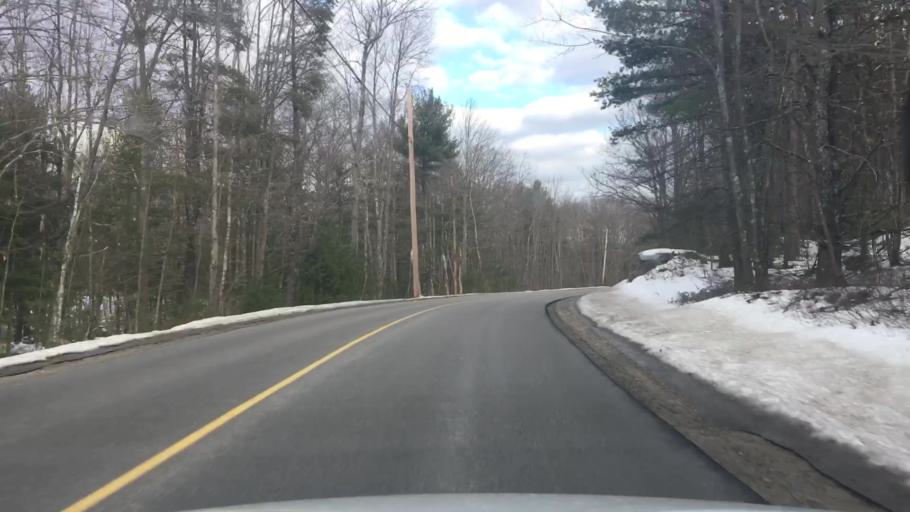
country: US
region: Maine
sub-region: York County
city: Arundel
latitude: 43.4093
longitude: -70.4819
